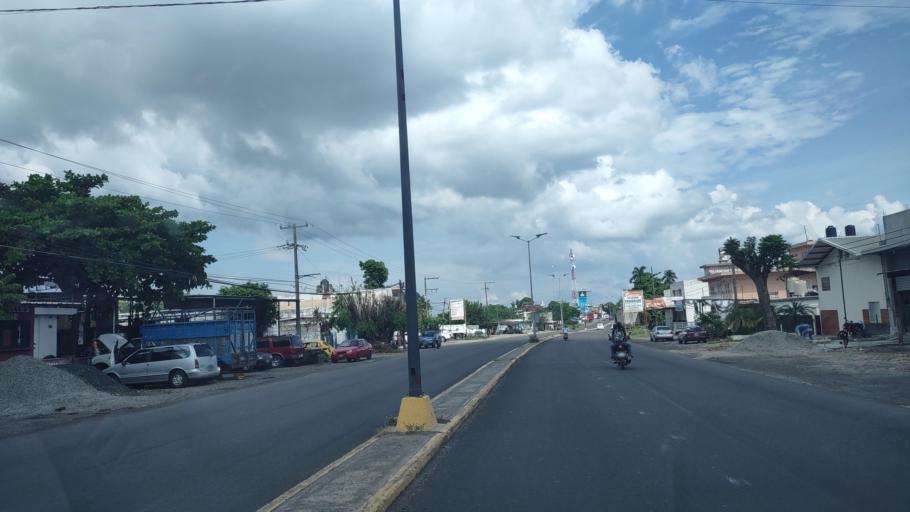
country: MX
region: Veracruz
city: Martinez de la Torre
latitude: 20.0716
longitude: -97.0679
